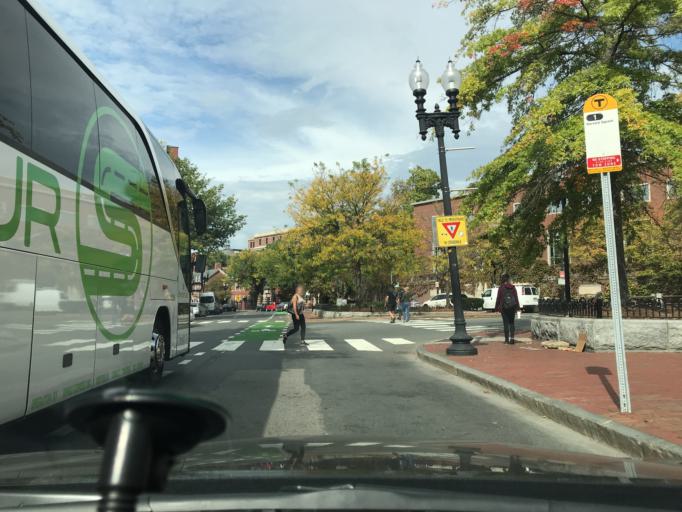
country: US
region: Massachusetts
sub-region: Middlesex County
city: Cambridge
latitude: 42.3721
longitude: -71.1153
